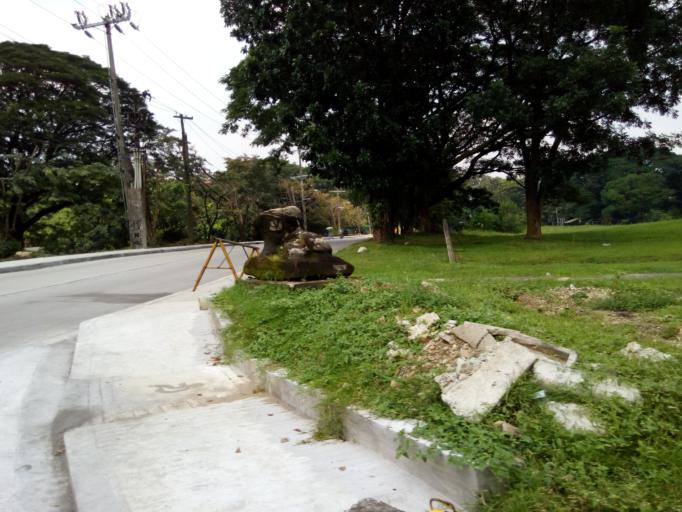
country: PH
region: Metro Manila
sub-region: Quezon City
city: Quezon City
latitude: 14.6551
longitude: 121.0625
